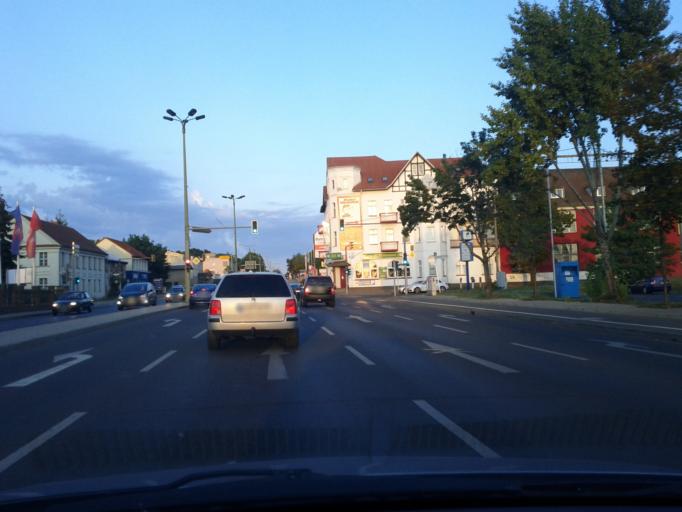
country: DE
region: Berlin
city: Kaulsdorf
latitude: 52.5051
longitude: 13.5805
